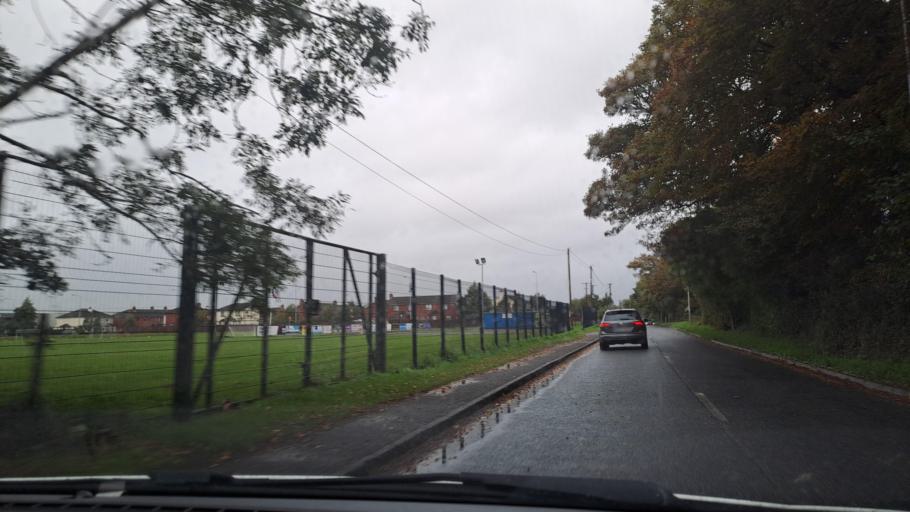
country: IE
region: Leinster
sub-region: Lu
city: Blackrock
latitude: 53.9869
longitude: -6.3709
